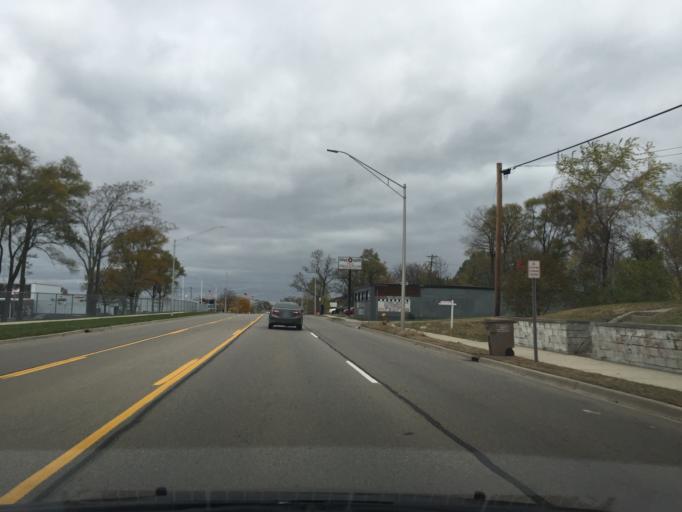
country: US
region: Michigan
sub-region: Oakland County
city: Pontiac
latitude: 42.6506
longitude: -83.3073
